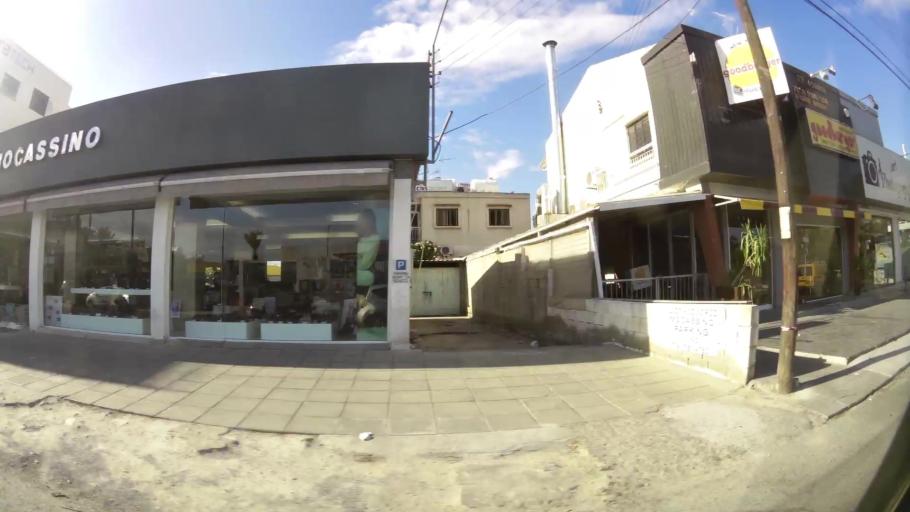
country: CY
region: Lefkosia
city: Nicosia
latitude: 35.1370
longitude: 33.3506
